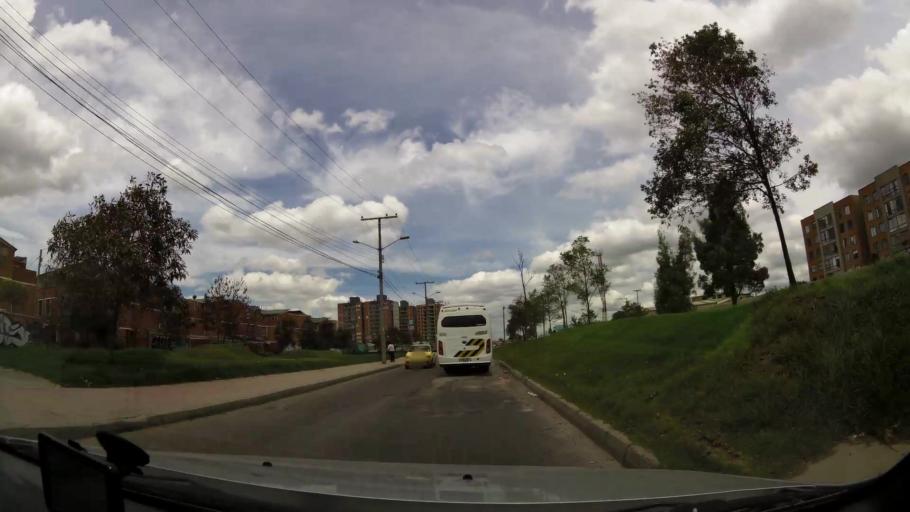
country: CO
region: Bogota D.C.
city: Bogota
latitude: 4.6523
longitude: -74.1509
